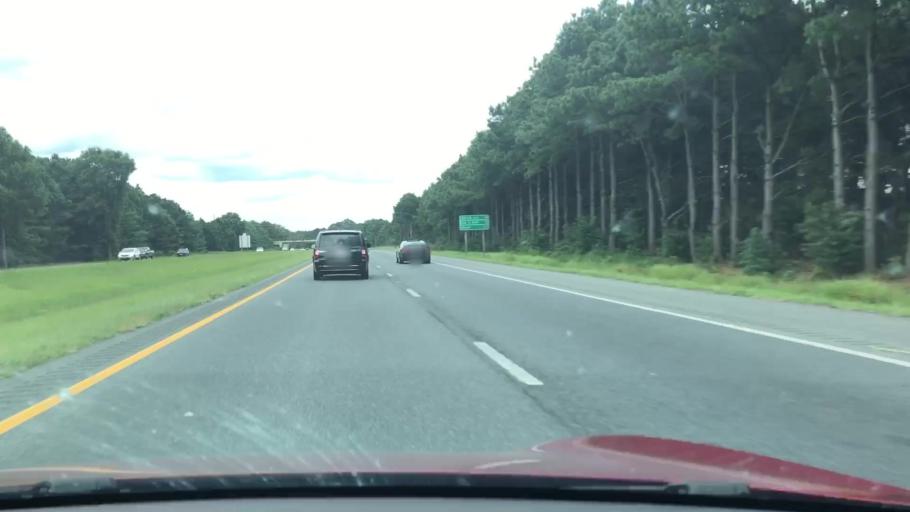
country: US
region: Maryland
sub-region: Wicomico County
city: Salisbury
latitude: 38.3390
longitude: -75.5551
